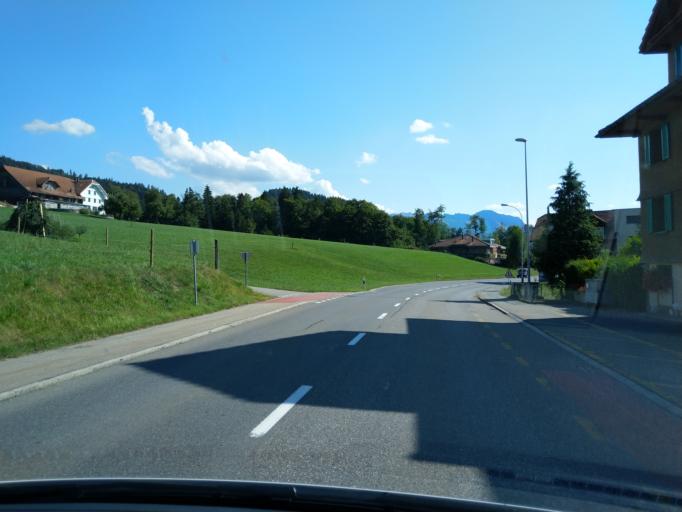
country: CH
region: Lucerne
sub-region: Entlebuch District
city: Entlebuch
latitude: 47.0080
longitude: 8.0734
